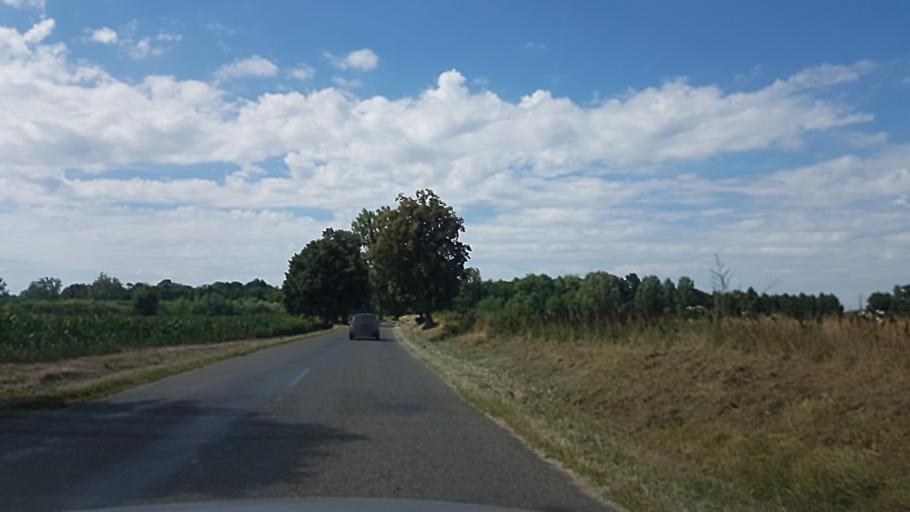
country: HU
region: Somogy
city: Barcs
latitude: 45.9577
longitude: 17.5973
